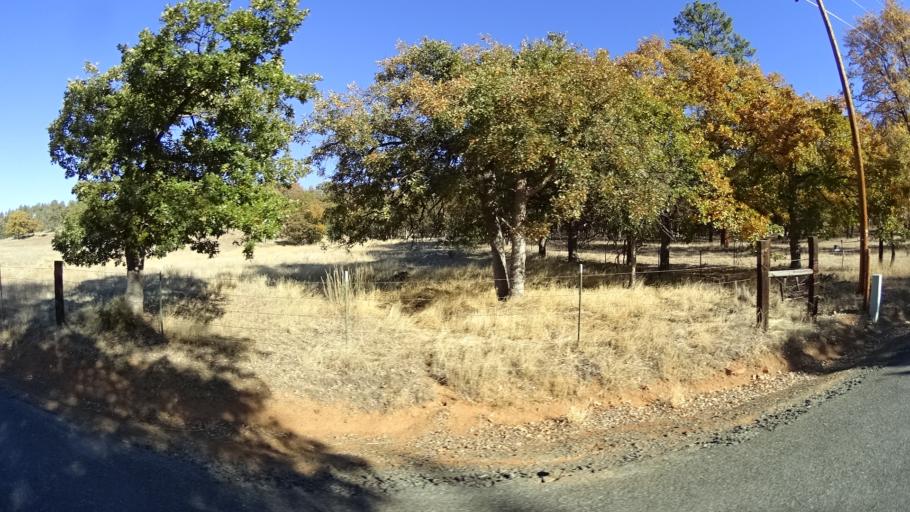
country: US
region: California
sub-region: Siskiyou County
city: Yreka
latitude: 41.5775
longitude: -122.8146
